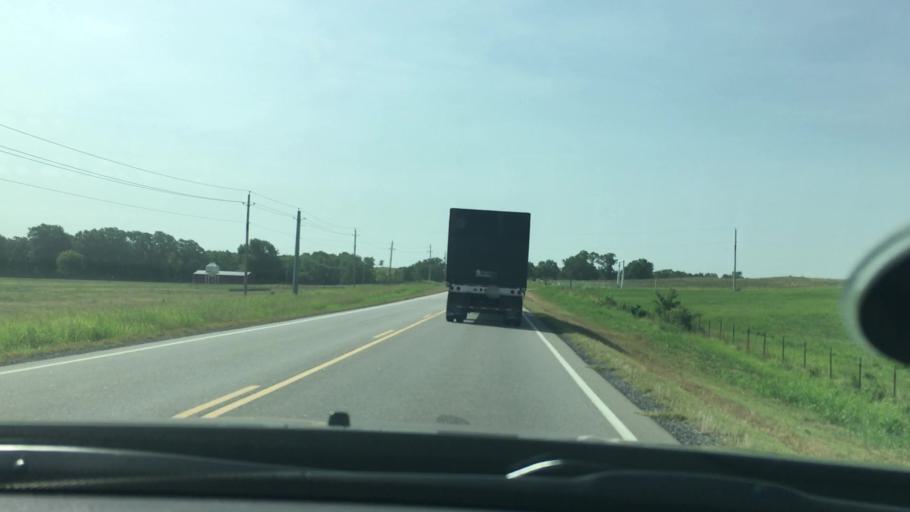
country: US
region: Oklahoma
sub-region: Atoka County
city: Atoka
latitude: 34.4091
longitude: -96.1819
